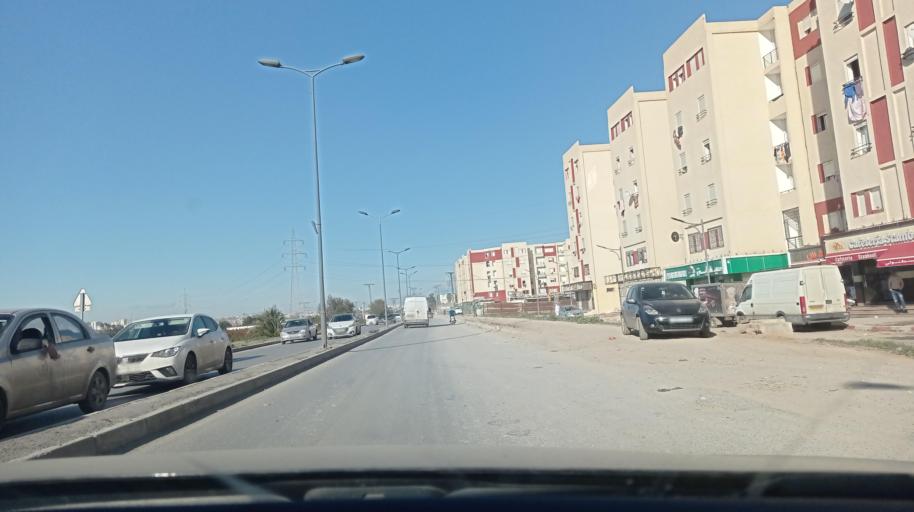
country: DZ
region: Tipaza
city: Baraki
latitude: 36.6619
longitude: 3.0855
